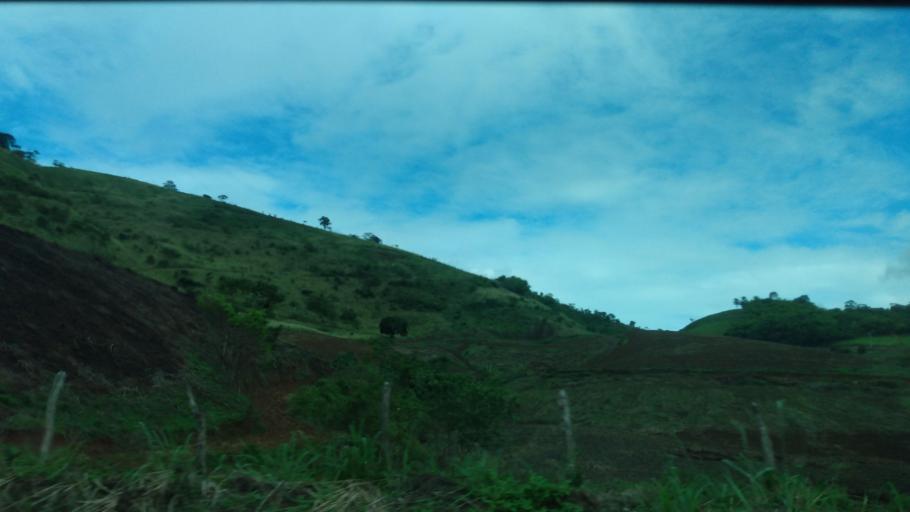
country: BR
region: Pernambuco
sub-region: Maraial
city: Maraial
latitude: -8.7248
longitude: -35.7877
